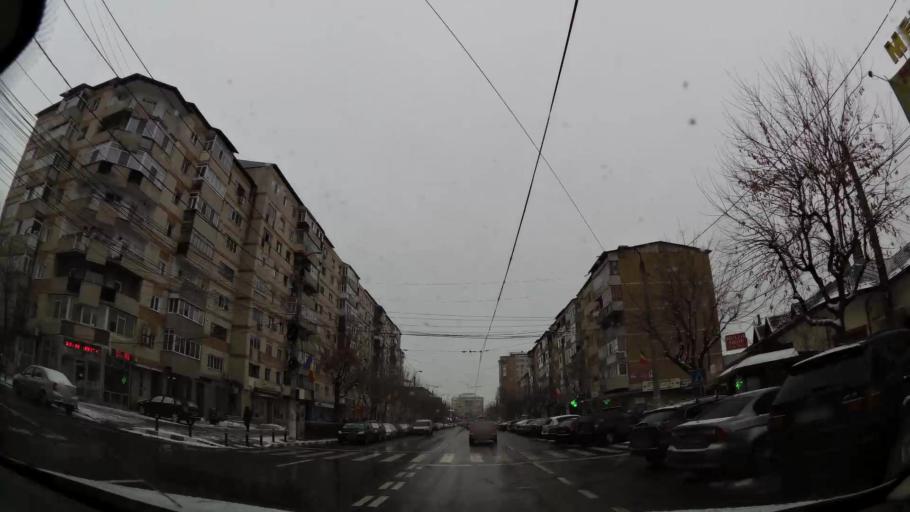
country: RO
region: Dambovita
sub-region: Municipiul Targoviste
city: Targoviste
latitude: 44.9237
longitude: 25.4655
